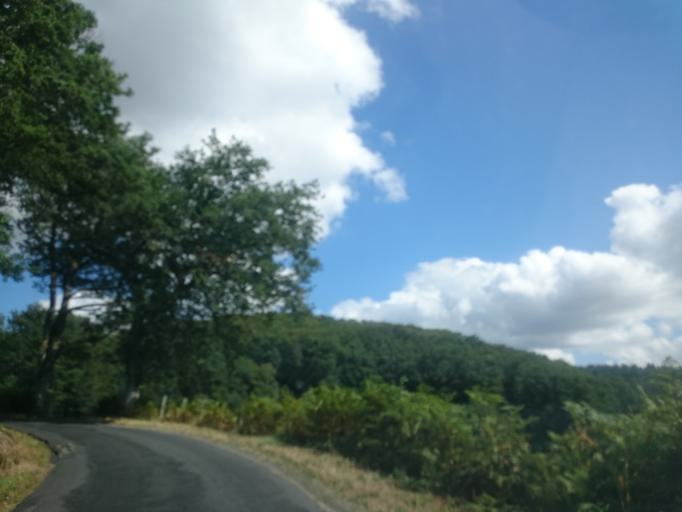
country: FR
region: Auvergne
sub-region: Departement du Cantal
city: Saint-Mamet-la-Salvetat
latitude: 44.8820
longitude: 2.2459
